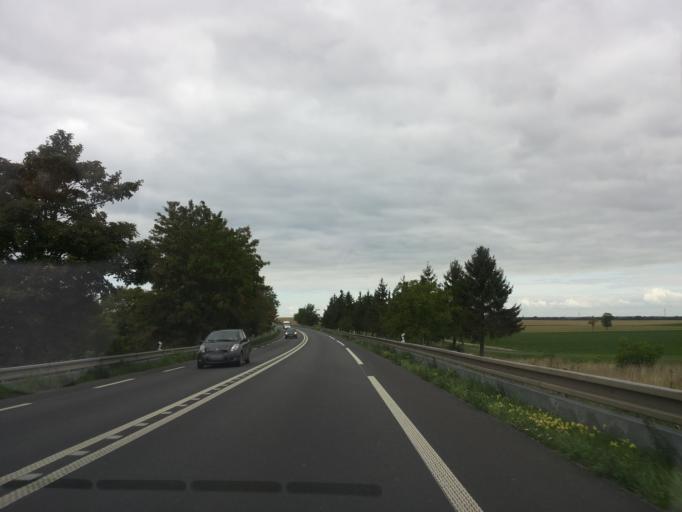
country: FR
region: Champagne-Ardenne
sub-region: Departement de la Marne
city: Verzy
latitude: 49.1365
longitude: 4.2306
